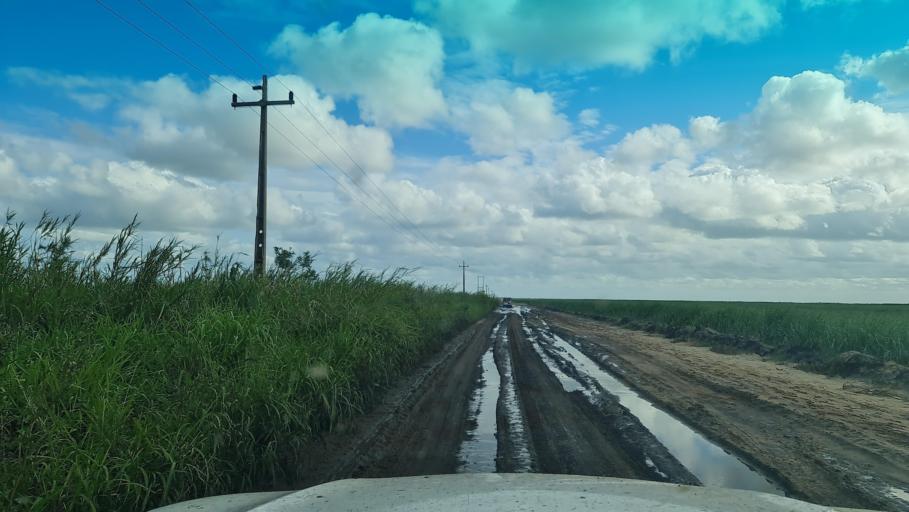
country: MZ
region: Maputo
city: Manhica
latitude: -25.4430
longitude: 32.8401
